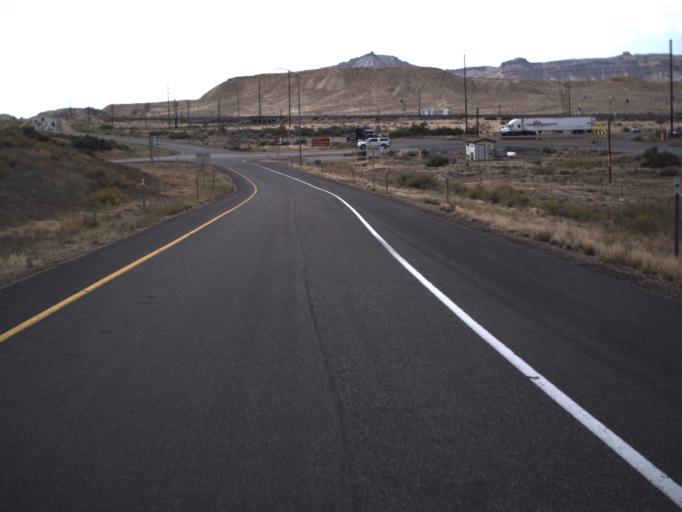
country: US
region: Utah
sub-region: Grand County
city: Moab
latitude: 38.9432
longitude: -109.8143
